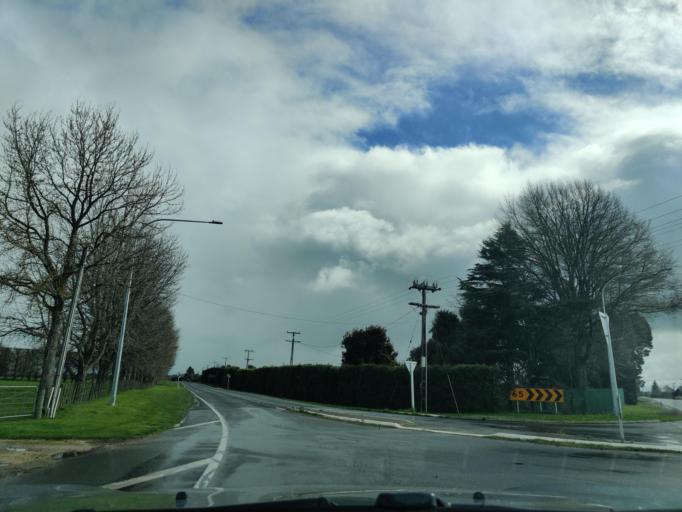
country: NZ
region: Hawke's Bay
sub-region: Hastings District
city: Hastings
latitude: -39.6778
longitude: 176.8337
